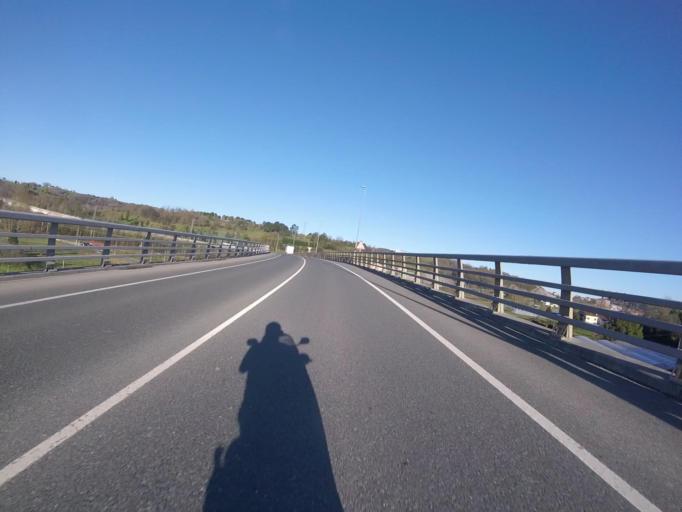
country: ES
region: Basque Country
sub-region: Provincia de Guipuzcoa
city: Astigarraga
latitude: 43.2875
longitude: -1.9516
